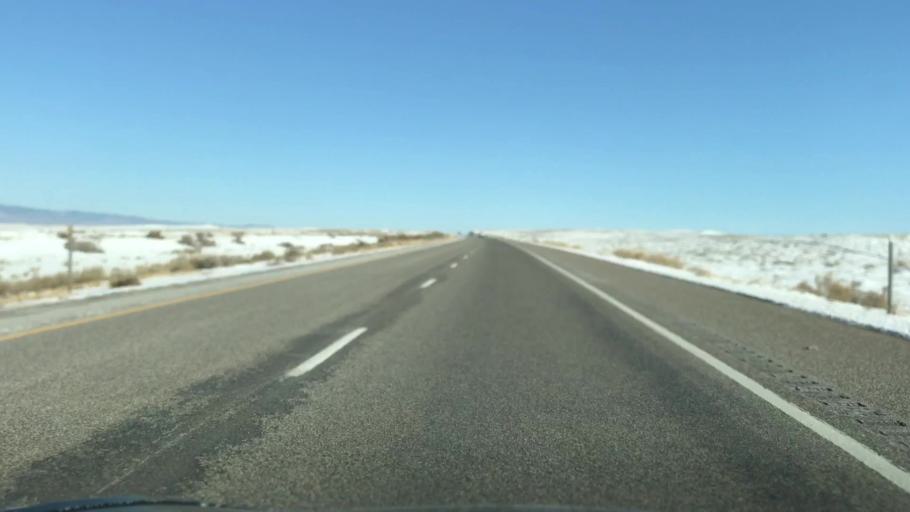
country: US
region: Colorado
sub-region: Mesa County
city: Loma
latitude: 39.1340
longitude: -109.1588
